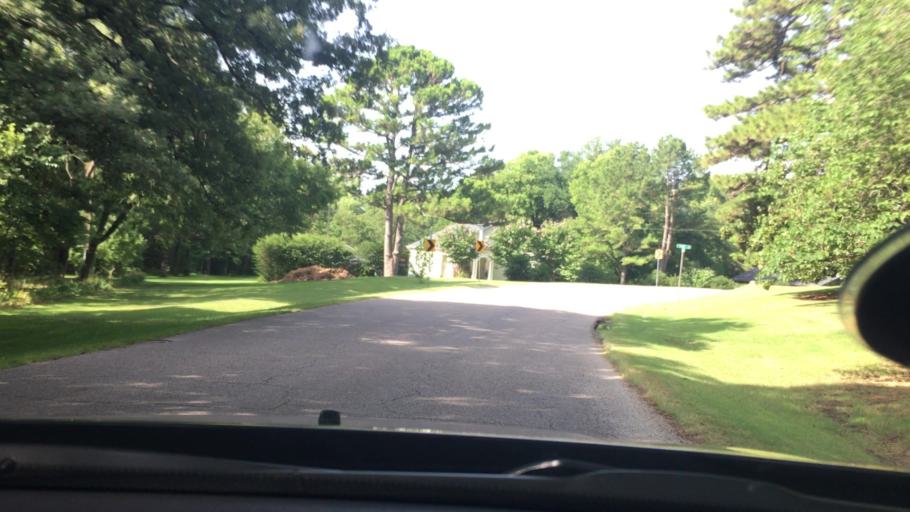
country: US
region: Oklahoma
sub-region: Pontotoc County
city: Ada
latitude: 34.7572
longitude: -96.6561
